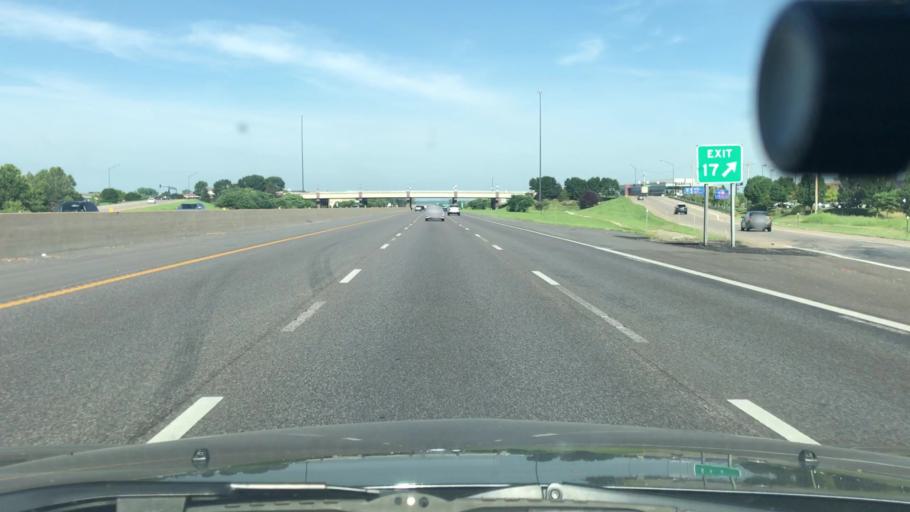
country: US
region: Missouri
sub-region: Saint Louis County
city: Chesterfield
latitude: 38.6703
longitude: -90.5953
